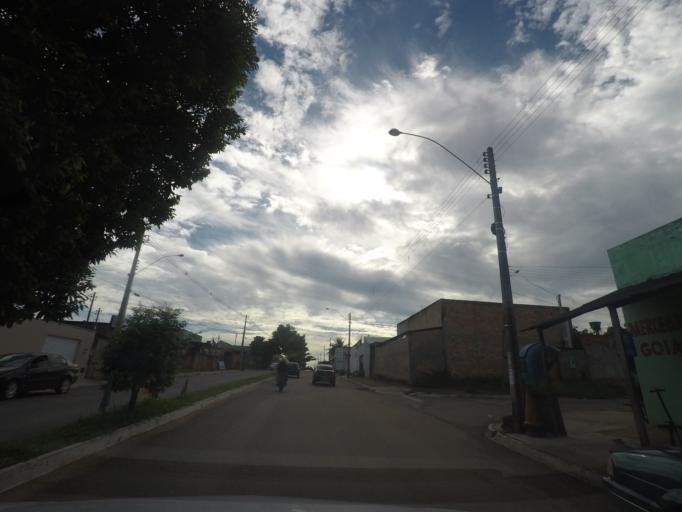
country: BR
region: Goias
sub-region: Aparecida De Goiania
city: Aparecida de Goiania
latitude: -16.8167
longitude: -49.3176
